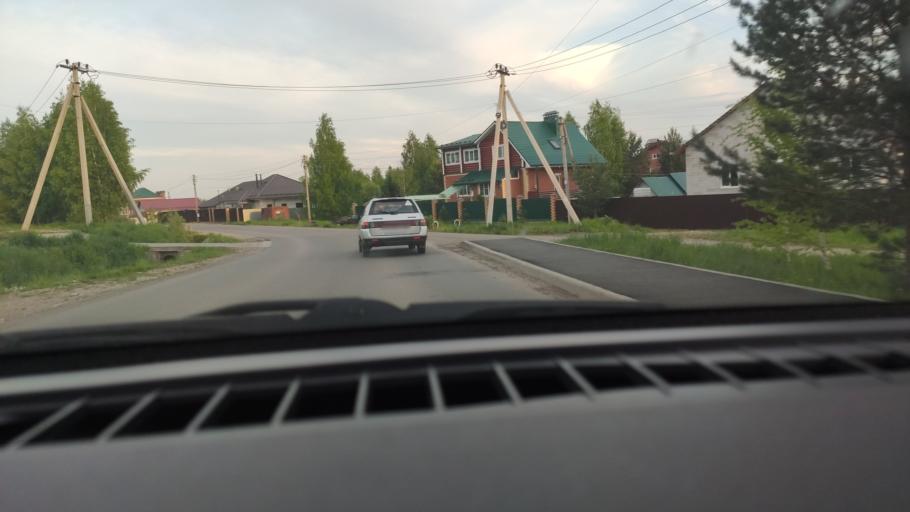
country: RU
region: Perm
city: Kondratovo
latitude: 58.0585
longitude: 56.0058
